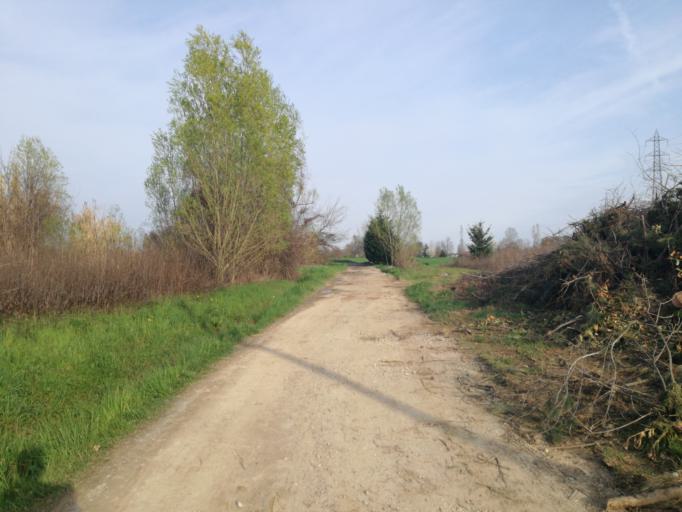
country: IT
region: Lombardy
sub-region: Provincia di Lecco
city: Verderio Superiore
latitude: 45.6691
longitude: 9.4516
